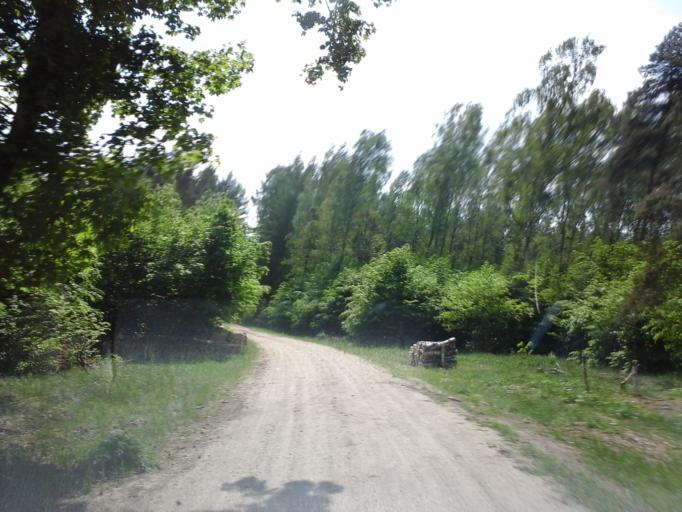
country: PL
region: West Pomeranian Voivodeship
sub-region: Powiat choszczenski
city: Drawno
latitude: 53.2380
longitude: 15.6702
